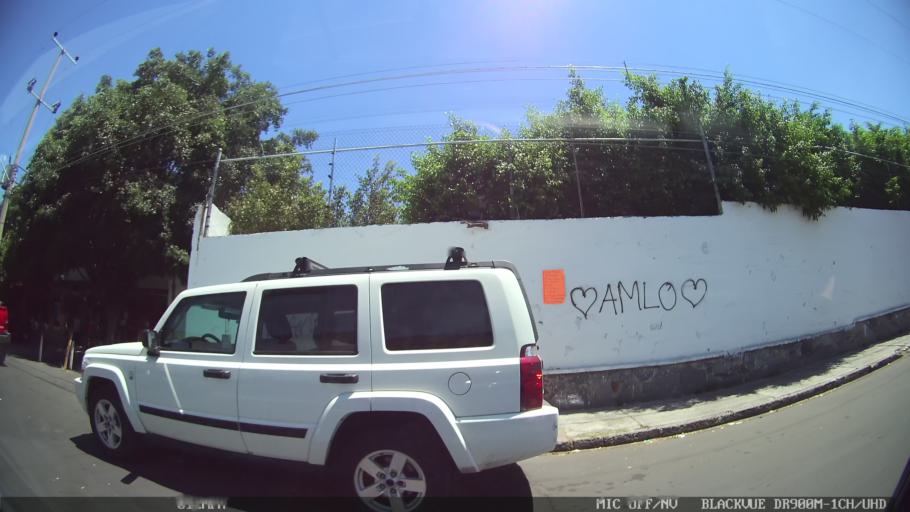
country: MX
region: Jalisco
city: Tlaquepaque
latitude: 20.6813
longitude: -103.2843
